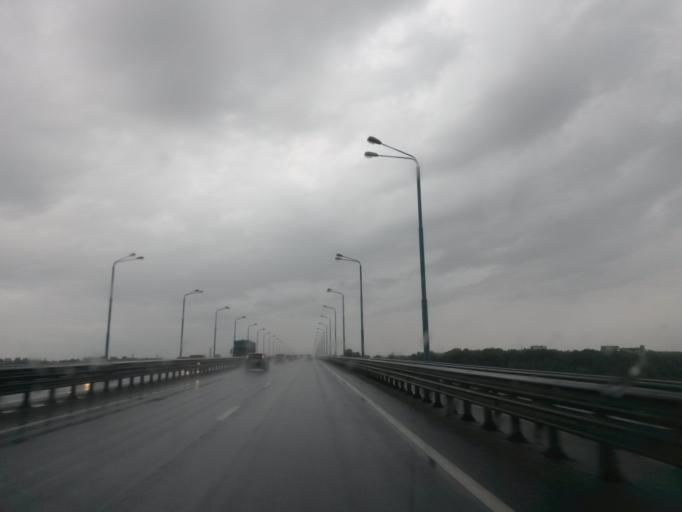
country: RU
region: Jaroslavl
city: Yaroslavl
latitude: 57.6757
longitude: 39.8589
